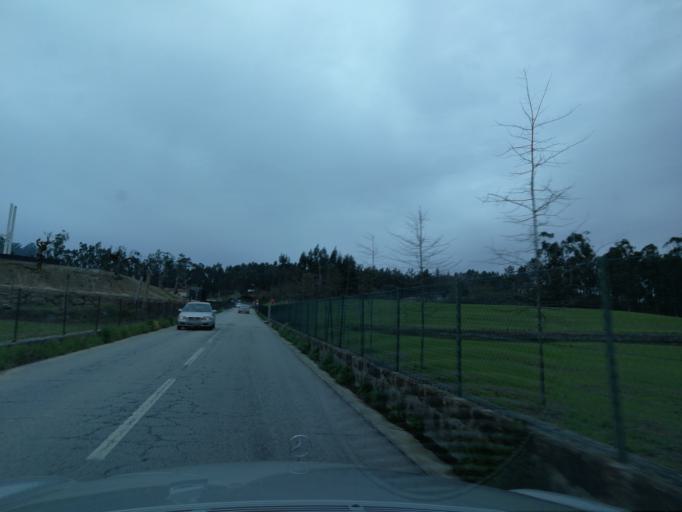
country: PT
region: Braga
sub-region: Braga
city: Oliveira
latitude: 41.4856
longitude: -8.4721
